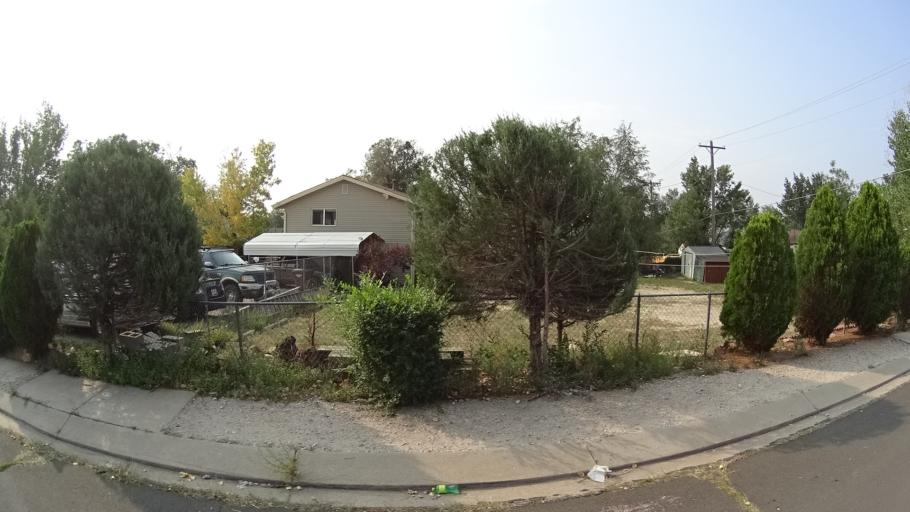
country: US
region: Colorado
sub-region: El Paso County
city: Stratmoor
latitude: 38.8033
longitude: -104.7668
